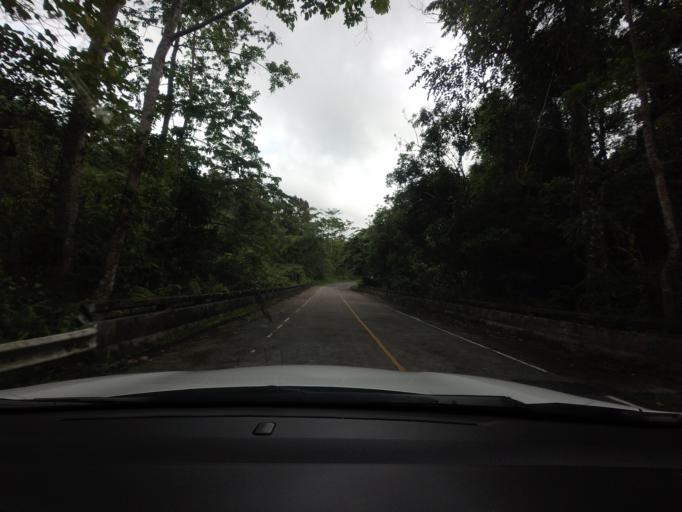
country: TH
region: Nakhon Nayok
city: Nakhon Nayok
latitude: 14.3594
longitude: 101.3453
